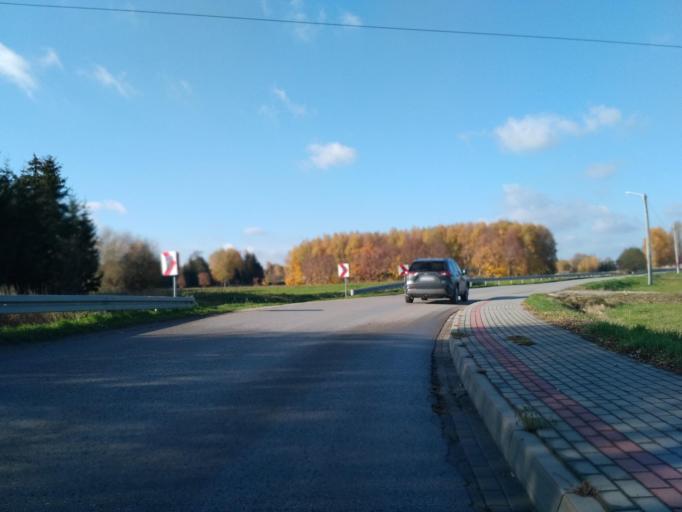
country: PL
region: Subcarpathian Voivodeship
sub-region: Powiat rzeszowski
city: Niechobrz
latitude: 50.0165
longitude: 21.8884
